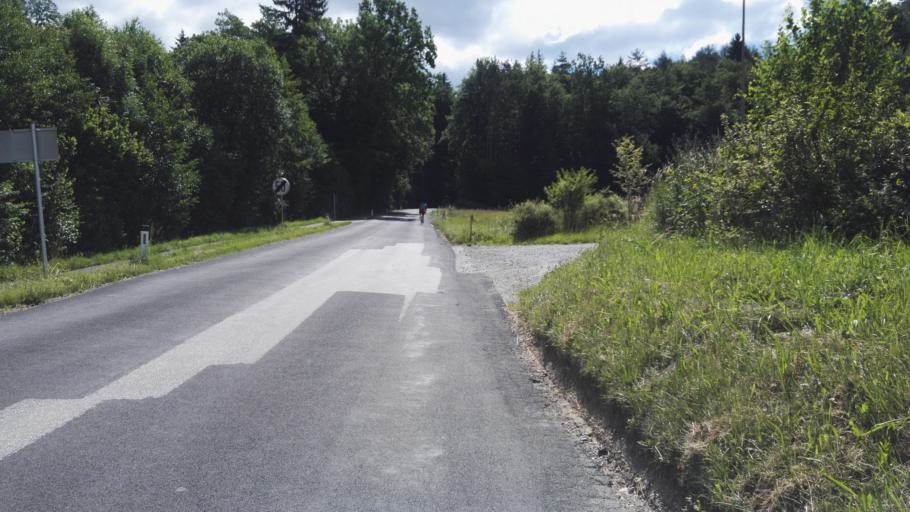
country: AT
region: Styria
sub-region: Politischer Bezirk Graz-Umgebung
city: Eggersdorf bei Graz
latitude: 47.0940
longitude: 15.5514
